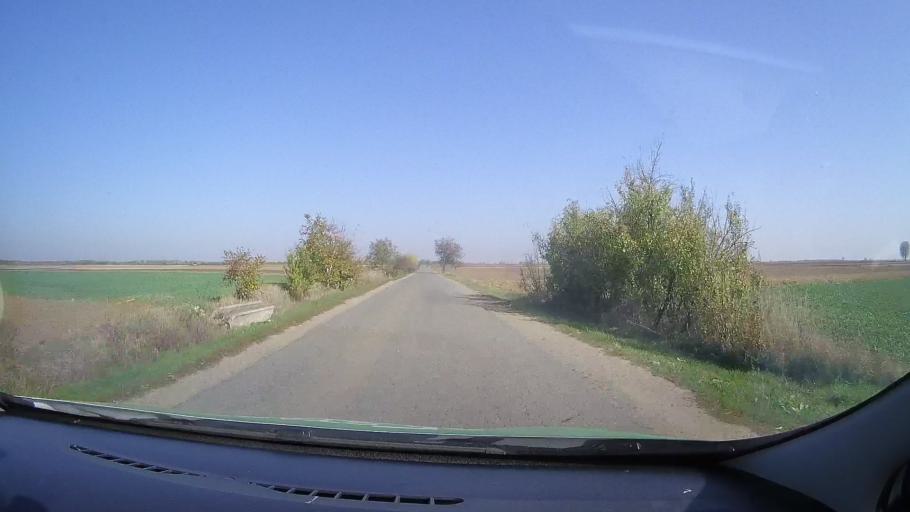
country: RO
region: Satu Mare
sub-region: Comuna Ciumesti
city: Ciumesti
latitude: 47.6731
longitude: 22.3428
